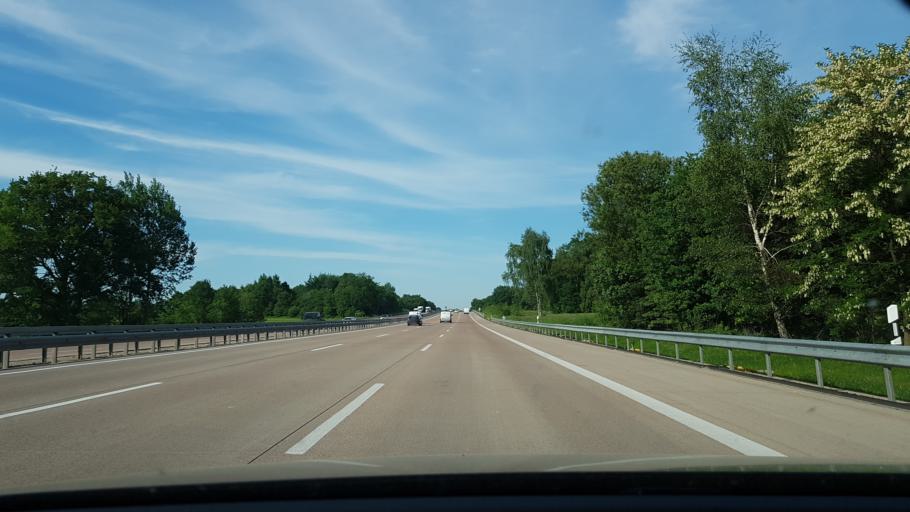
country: DE
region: Schleswig-Holstein
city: Stapelfeld
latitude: 53.5924
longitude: 10.2186
